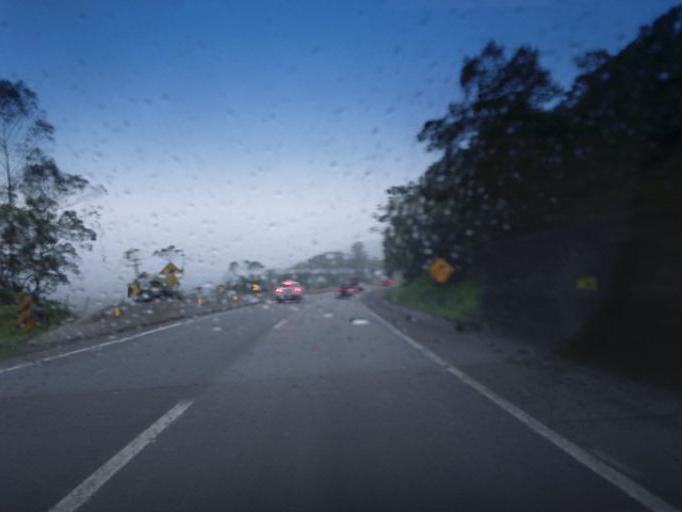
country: BR
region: Parana
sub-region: Guaratuba
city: Guaratuba
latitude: -25.9279
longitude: -48.9130
